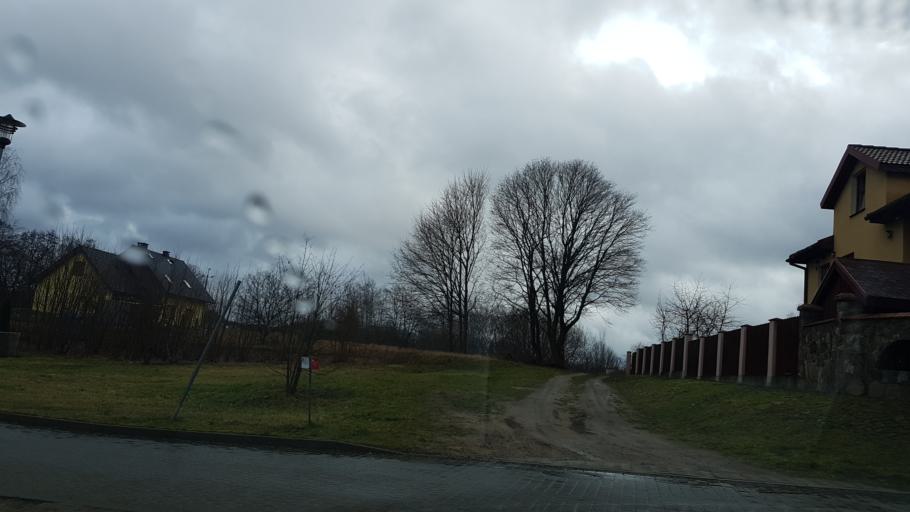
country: PL
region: West Pomeranian Voivodeship
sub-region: Powiat drawski
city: Czaplinek
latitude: 53.5509
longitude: 16.2469
